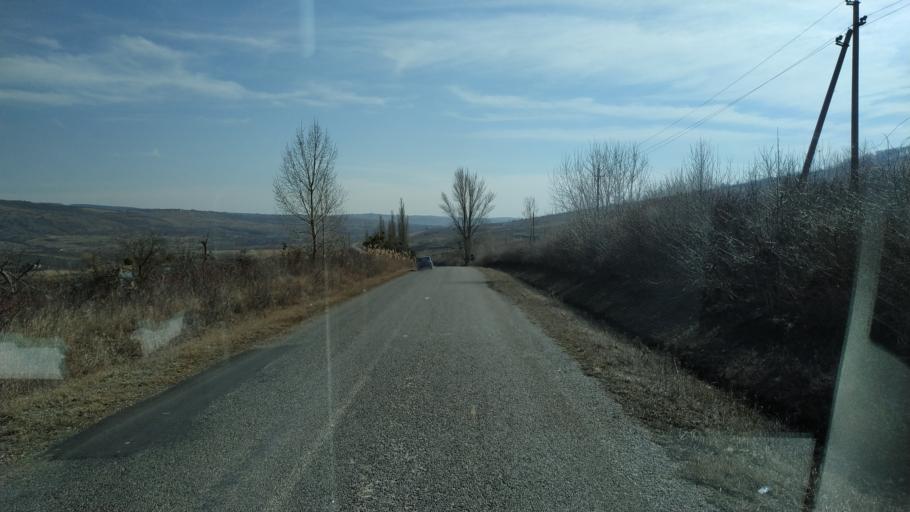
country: MD
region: Nisporeni
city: Nisporeni
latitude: 47.1739
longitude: 28.0878
